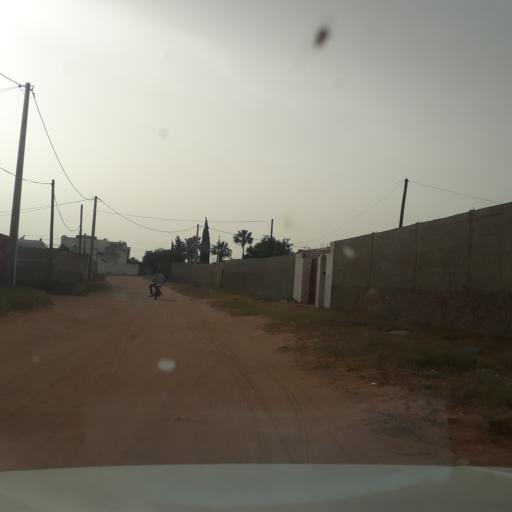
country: TN
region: Safaqis
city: Al Qarmadah
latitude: 34.8185
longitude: 10.7712
